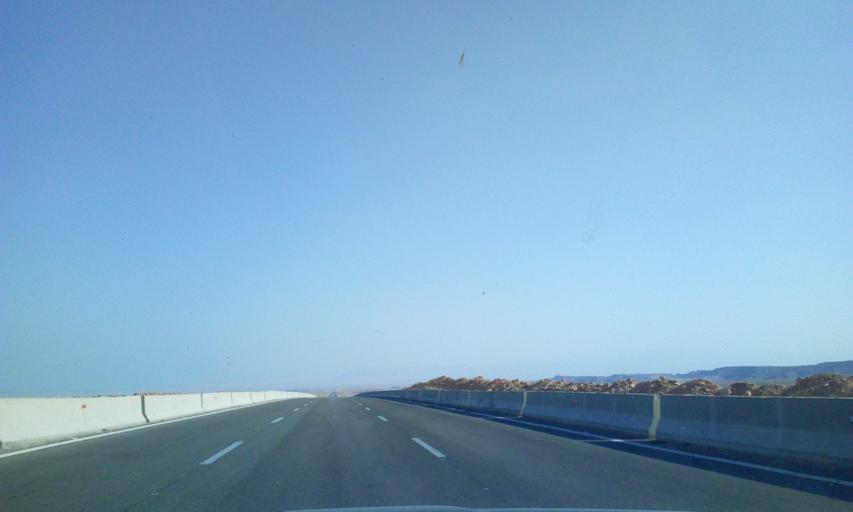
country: EG
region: As Suways
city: Ain Sukhna
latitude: 29.2611
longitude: 32.4741
